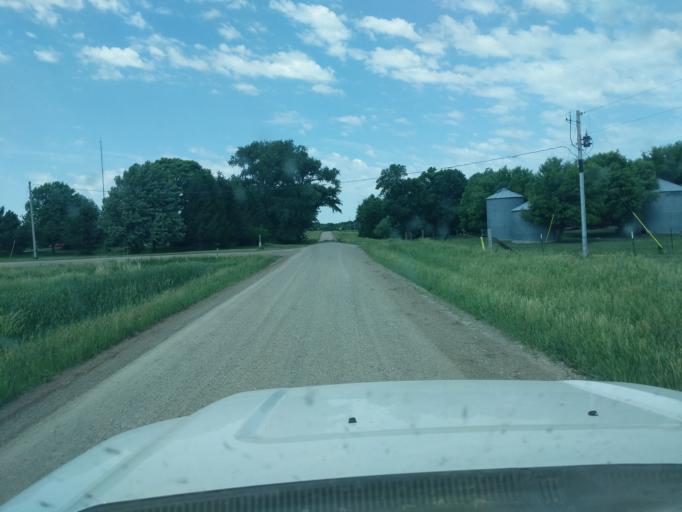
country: US
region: Minnesota
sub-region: Yellow Medicine County
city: Granite Falls
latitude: 44.7453
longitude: -95.3965
